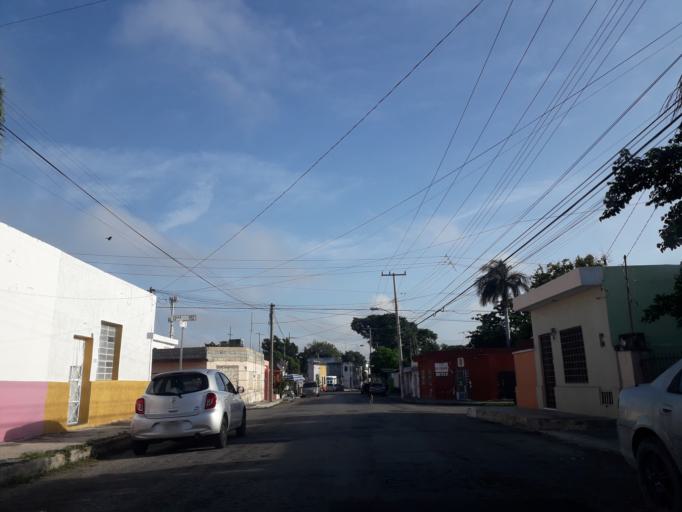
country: MX
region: Yucatan
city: Merida
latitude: 20.9645
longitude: -89.6407
